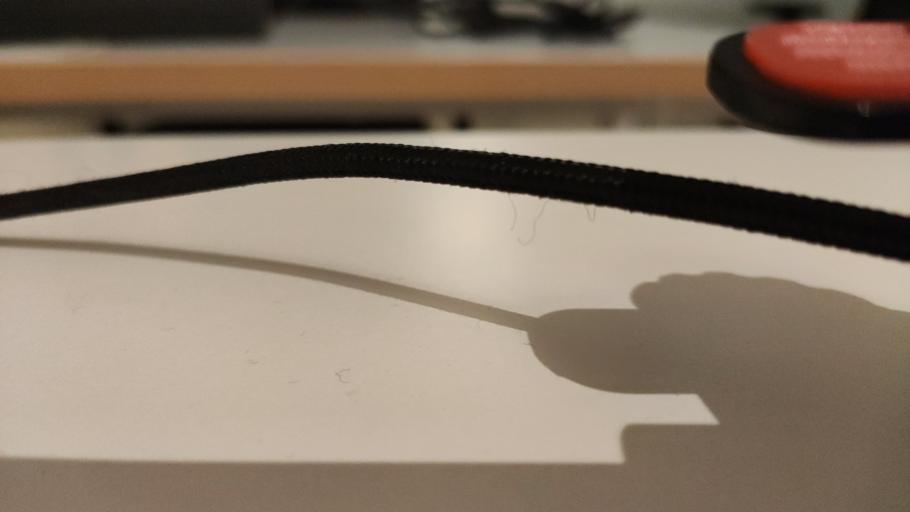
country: RU
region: Moskovskaya
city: Shemetovo
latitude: 56.4144
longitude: 37.9914
